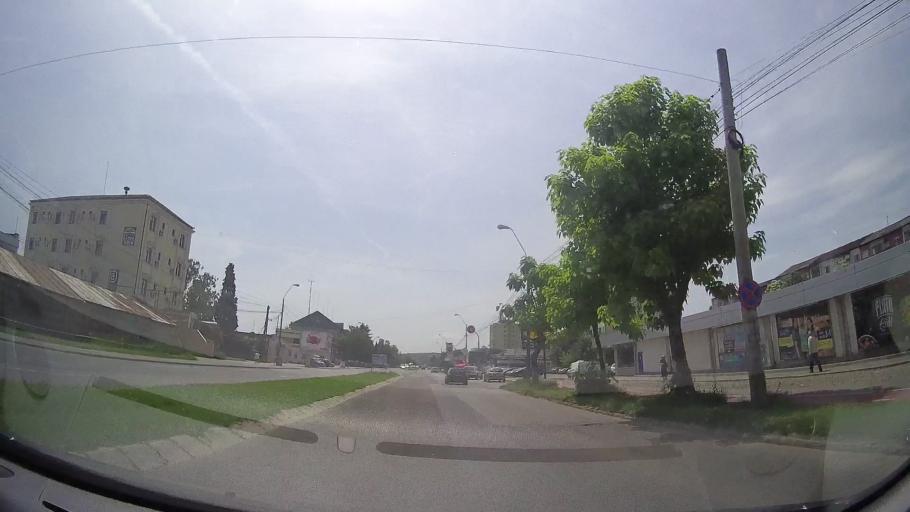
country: RO
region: Hunedoara
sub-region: Municipiul Deva
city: Deva
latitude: 45.8777
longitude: 22.9145
